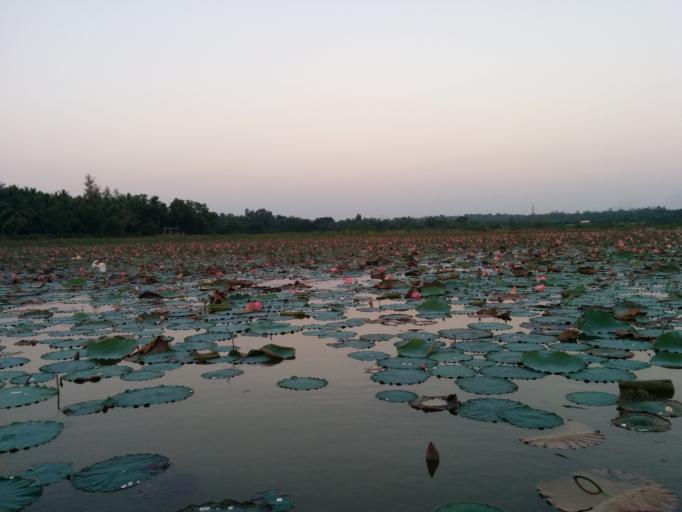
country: IN
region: Tamil Nadu
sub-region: Villupuram
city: Auroville
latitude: 11.9545
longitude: 79.7524
